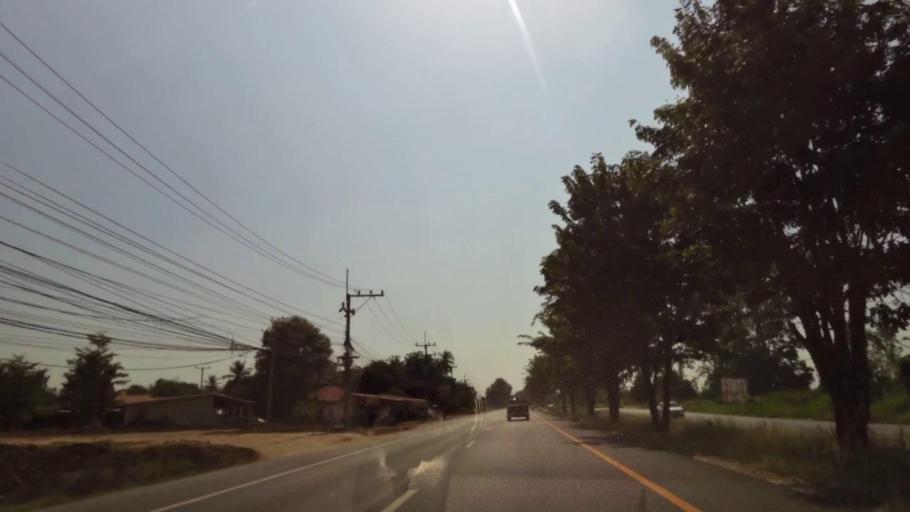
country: TH
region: Nakhon Sawan
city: Kao Liao
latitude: 15.9578
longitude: 100.1180
